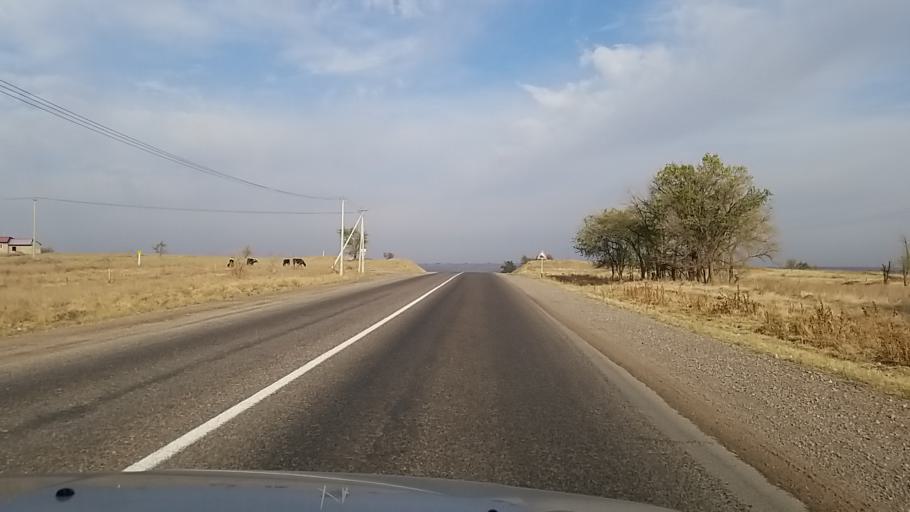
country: KZ
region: Almaty Oblysy
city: Burunday
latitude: 43.4856
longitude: 76.6722
